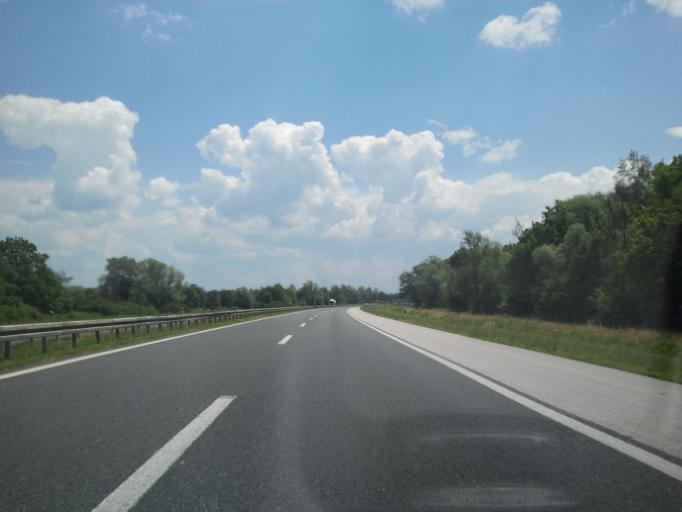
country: HR
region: Sisacko-Moslavacka
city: Husain
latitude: 45.4464
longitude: 16.8108
